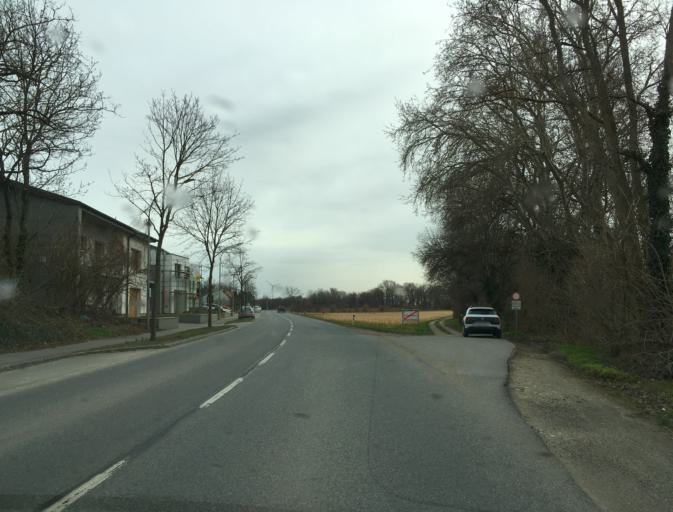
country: AT
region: Lower Austria
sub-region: Politischer Bezirk Ganserndorf
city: Deutsch-Wagram
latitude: 48.2924
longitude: 16.5609
